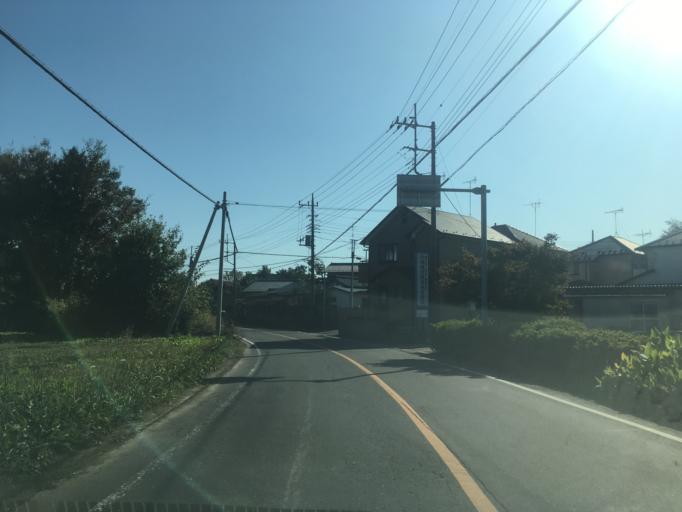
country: JP
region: Saitama
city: Sakado
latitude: 35.9611
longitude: 139.4454
